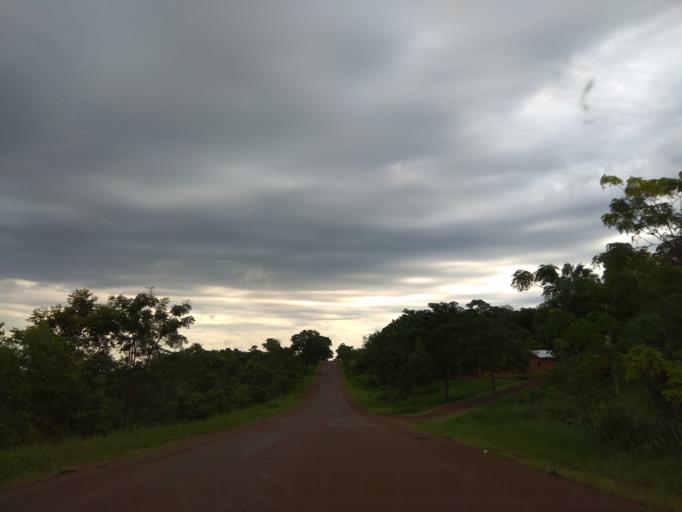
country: AR
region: Misiones
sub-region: Departamento de Leandro N. Alem
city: Leandro N. Alem
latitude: -27.5947
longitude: -55.3542
